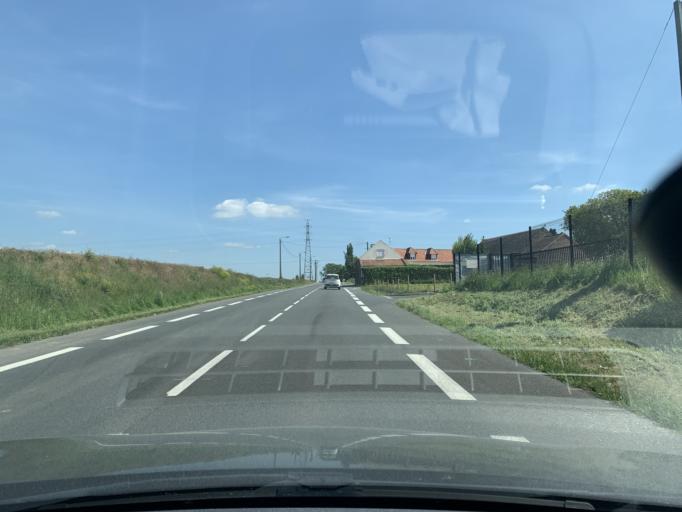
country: FR
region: Nord-Pas-de-Calais
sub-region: Departement du Nord
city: Fontaine-au-Pire
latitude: 50.1288
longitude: 3.3909
